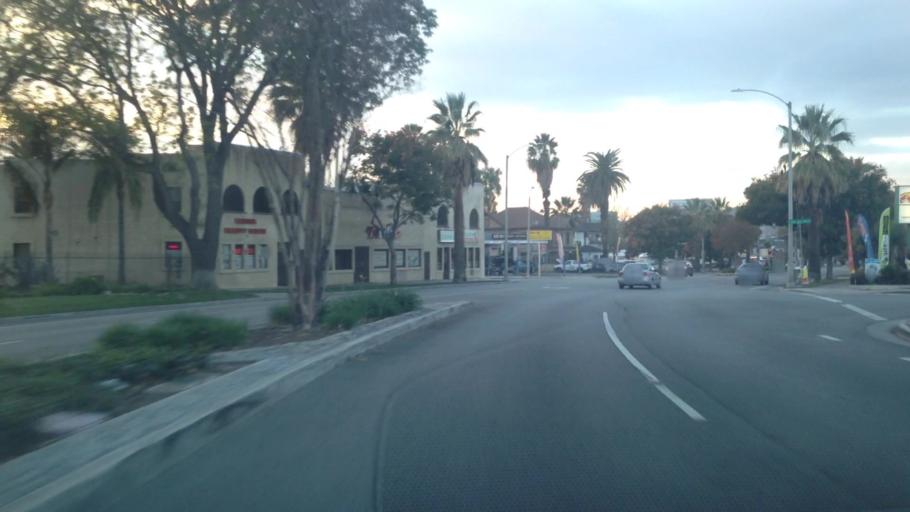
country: US
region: California
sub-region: Riverside County
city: Riverside
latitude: 33.9756
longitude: -117.3606
